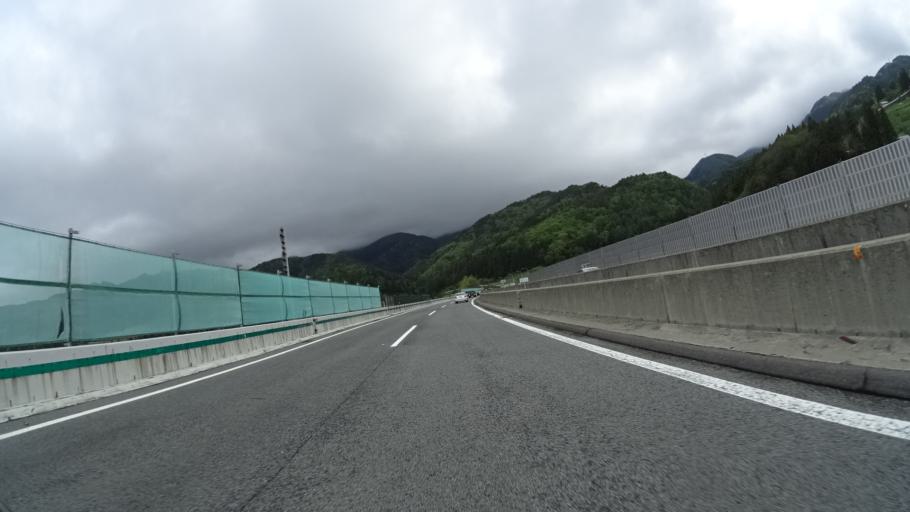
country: JP
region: Nagano
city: Nagano-shi
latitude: 36.5199
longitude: 138.0749
